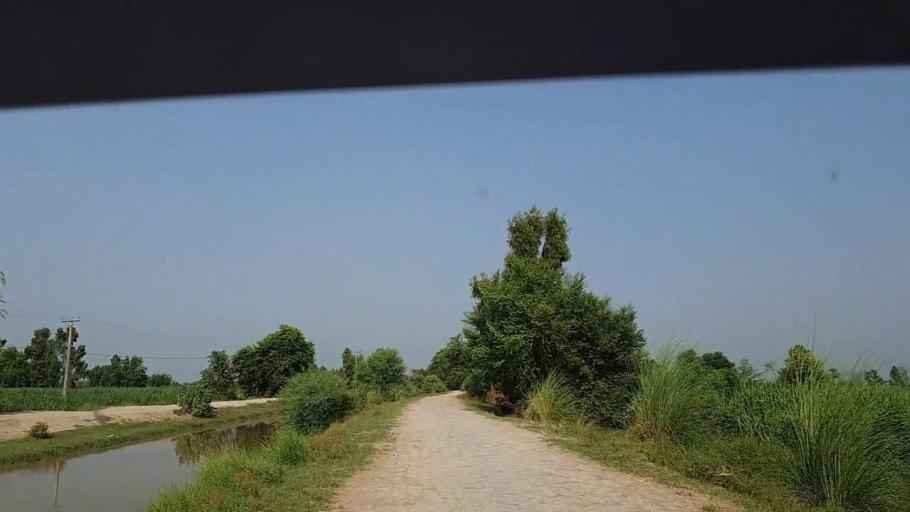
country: PK
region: Sindh
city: Adilpur
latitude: 27.9684
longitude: 69.3130
